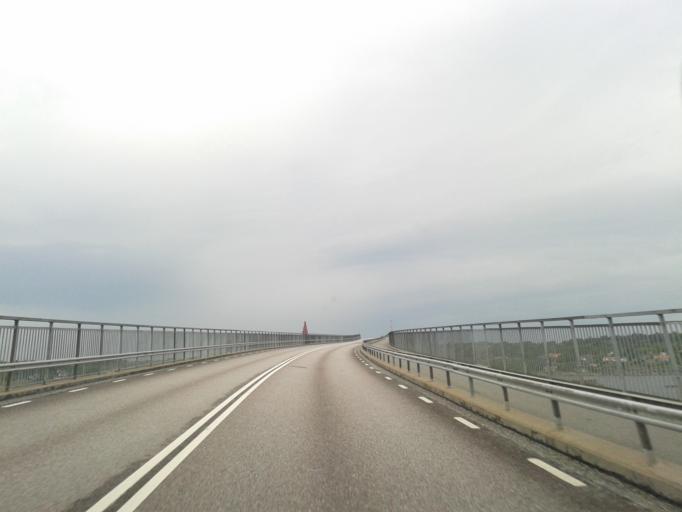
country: SE
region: Vaestra Goetaland
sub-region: Kungalvs Kommun
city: Marstrand
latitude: 57.8898
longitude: 11.6658
